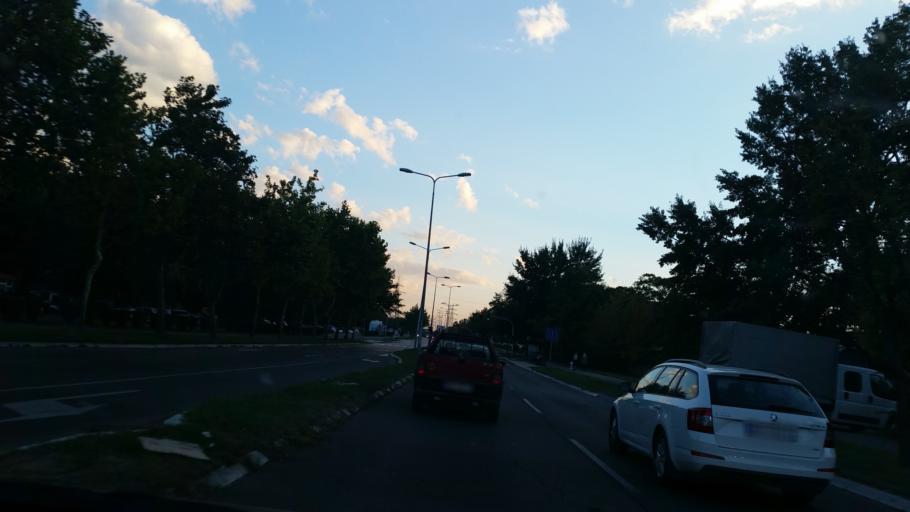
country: RS
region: Central Serbia
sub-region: Belgrade
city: Zemun
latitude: 44.8234
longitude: 20.3892
